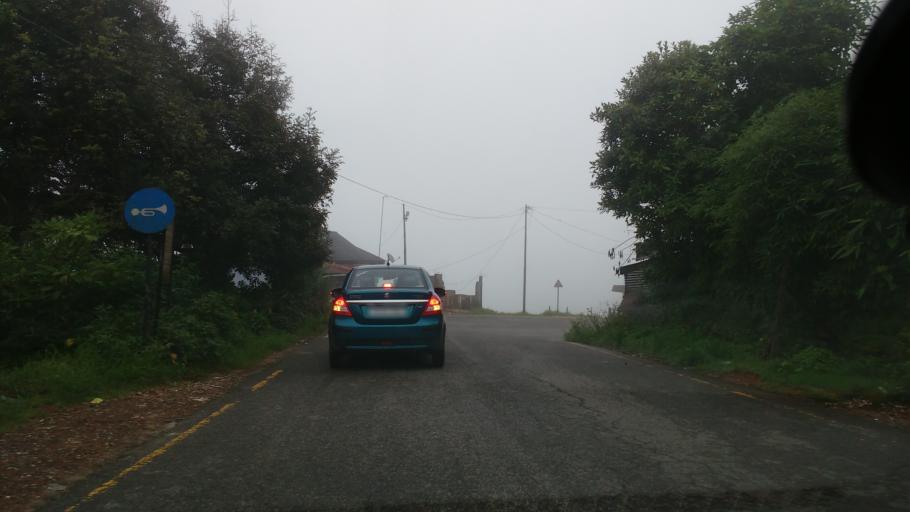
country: IN
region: Meghalaya
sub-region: East Khasi Hills
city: Cherrapunji
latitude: 25.2863
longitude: 91.7195
